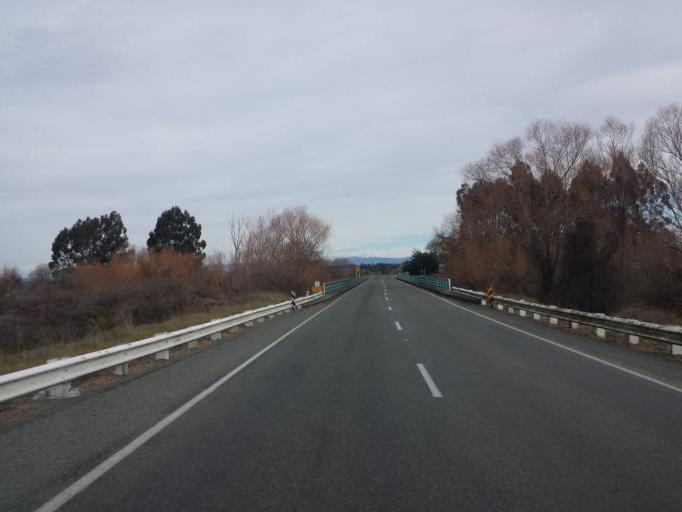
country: NZ
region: Canterbury
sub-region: Timaru District
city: Pleasant Point
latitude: -44.1161
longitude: 171.2106
